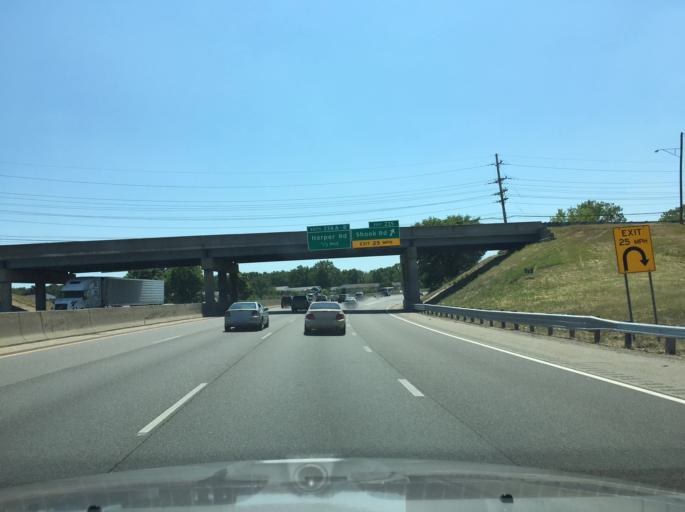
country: US
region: Michigan
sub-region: Macomb County
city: Mount Clemens
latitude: 42.5568
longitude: -82.8599
